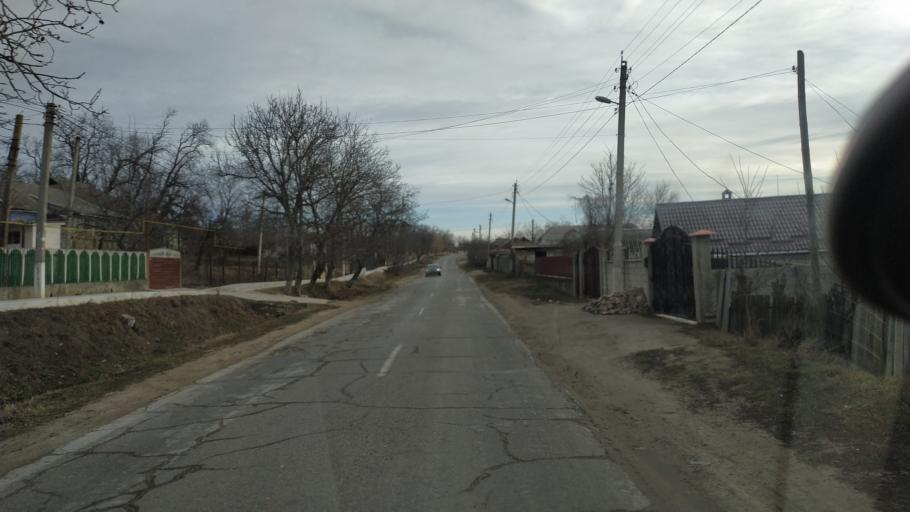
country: MD
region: Chisinau
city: Vadul lui Voda
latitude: 47.1467
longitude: 29.0773
